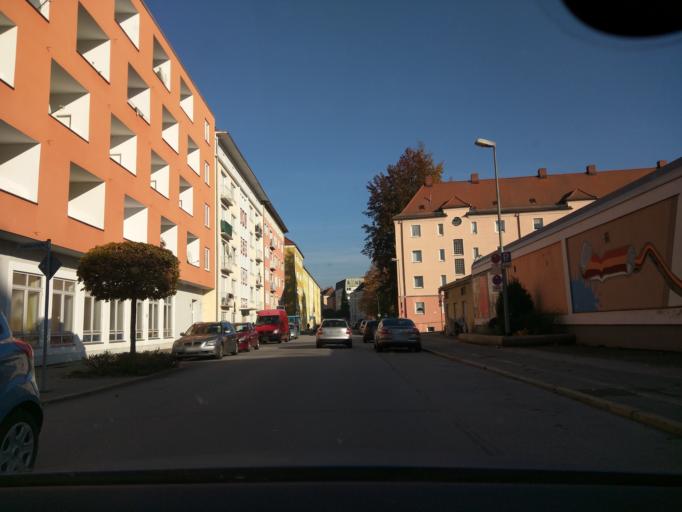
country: DE
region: Bavaria
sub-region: Lower Bavaria
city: Passau
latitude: 48.5710
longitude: 13.4383
